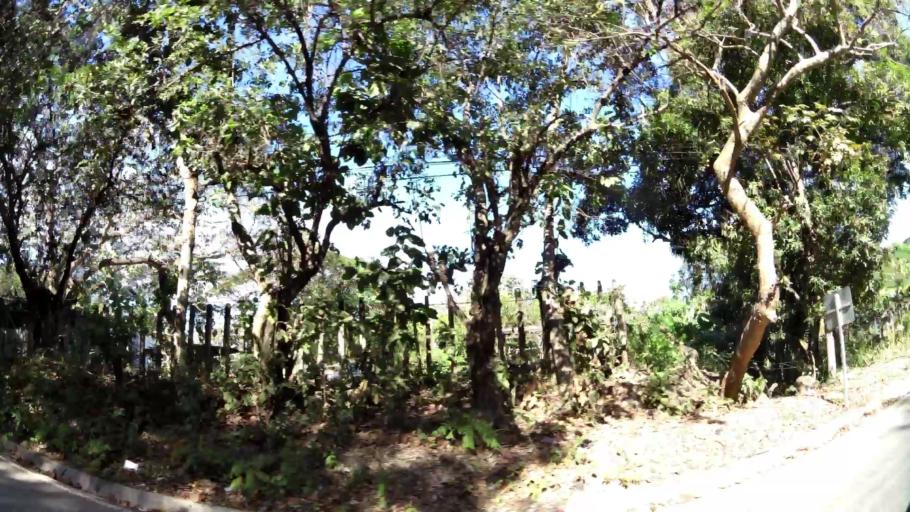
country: SV
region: Cuscatlan
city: Suchitoto
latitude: 13.9322
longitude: -89.0278
